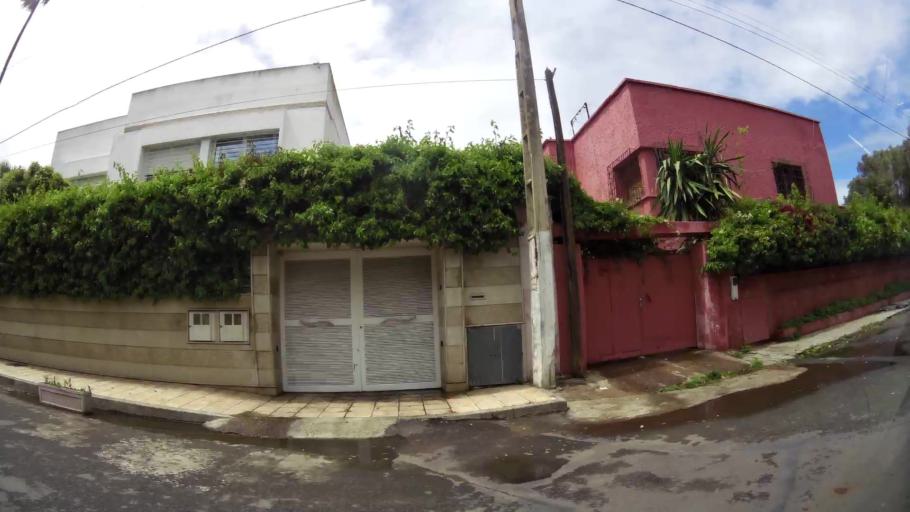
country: MA
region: Grand Casablanca
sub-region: Casablanca
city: Casablanca
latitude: 33.5655
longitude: -7.6298
